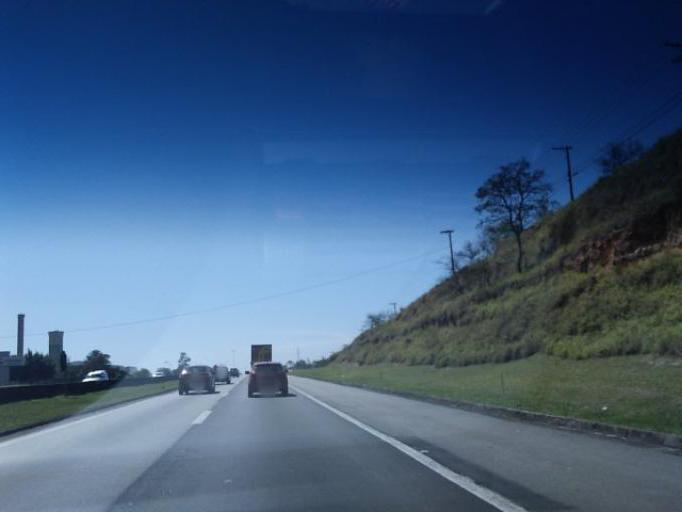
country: BR
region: Sao Paulo
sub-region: Cacapava
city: Cacapava
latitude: -23.1363
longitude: -45.7539
